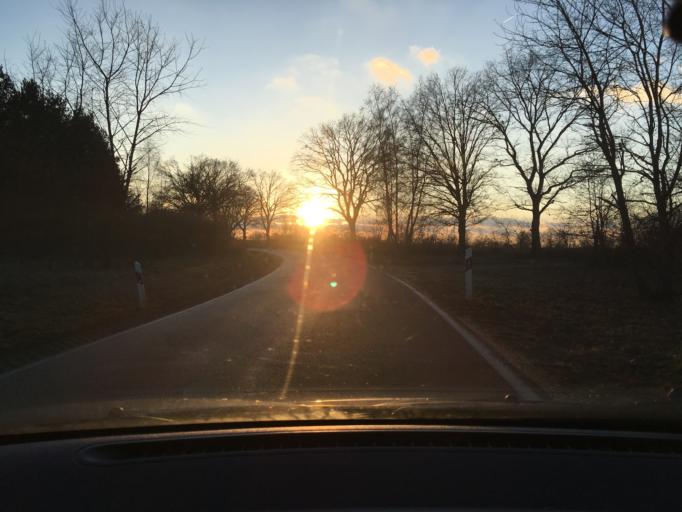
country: DE
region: Schleswig-Holstein
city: Brothen
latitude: 53.4852
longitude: 10.6739
